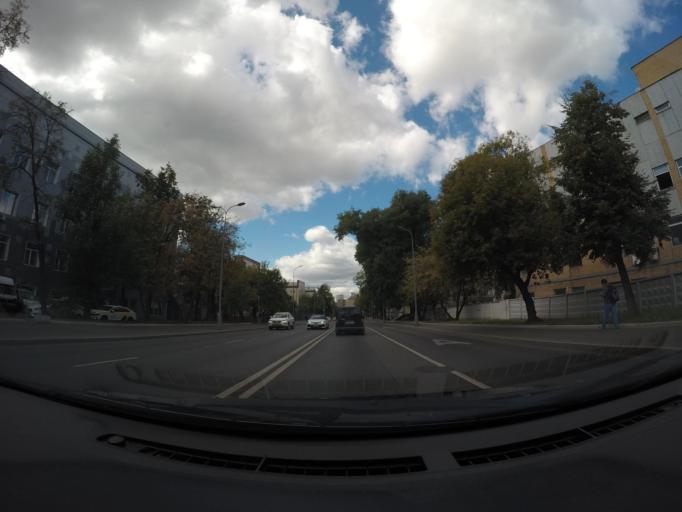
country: RU
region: Moscow
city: Lefortovo
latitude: 55.7812
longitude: 37.7146
